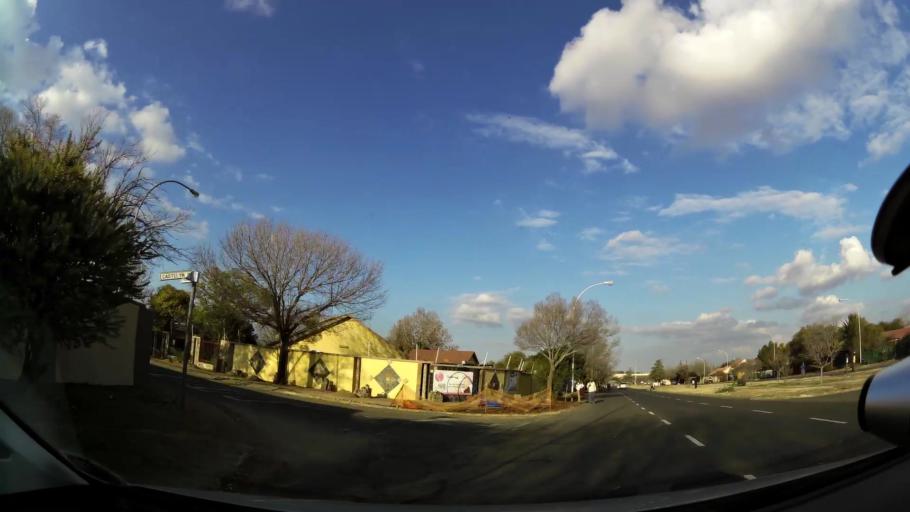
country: ZA
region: Orange Free State
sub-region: Mangaung Metropolitan Municipality
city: Bloemfontein
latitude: -29.1527
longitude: 26.1810
